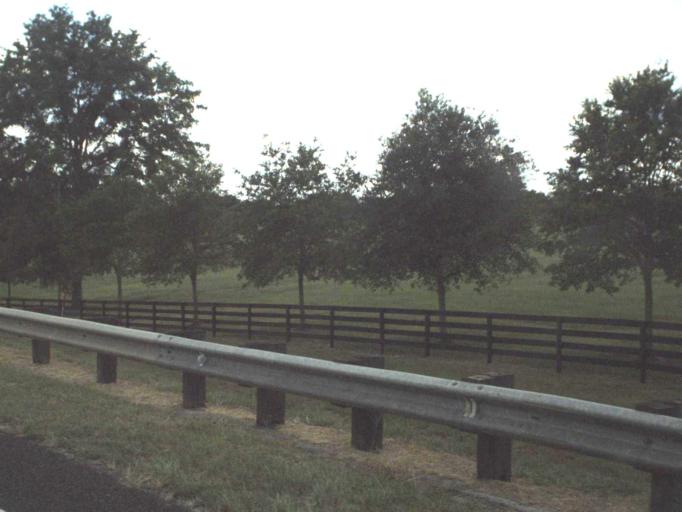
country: US
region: Florida
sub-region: Marion County
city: Citra
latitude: 29.3157
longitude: -82.1518
